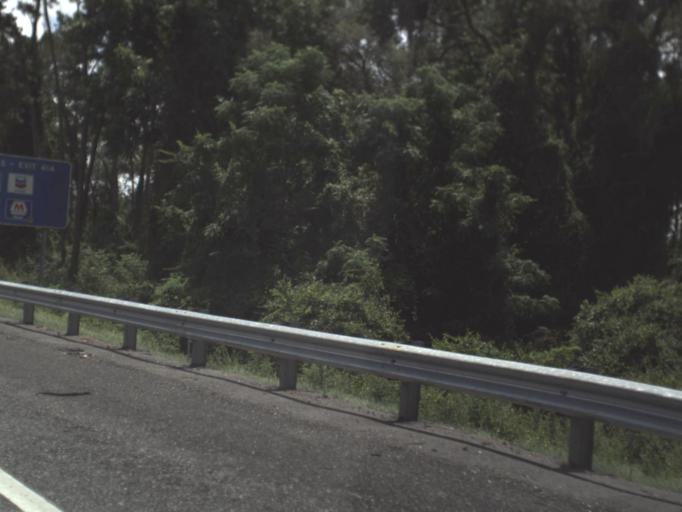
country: US
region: Florida
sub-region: Alachua County
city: High Springs
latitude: 30.0036
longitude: -82.6031
